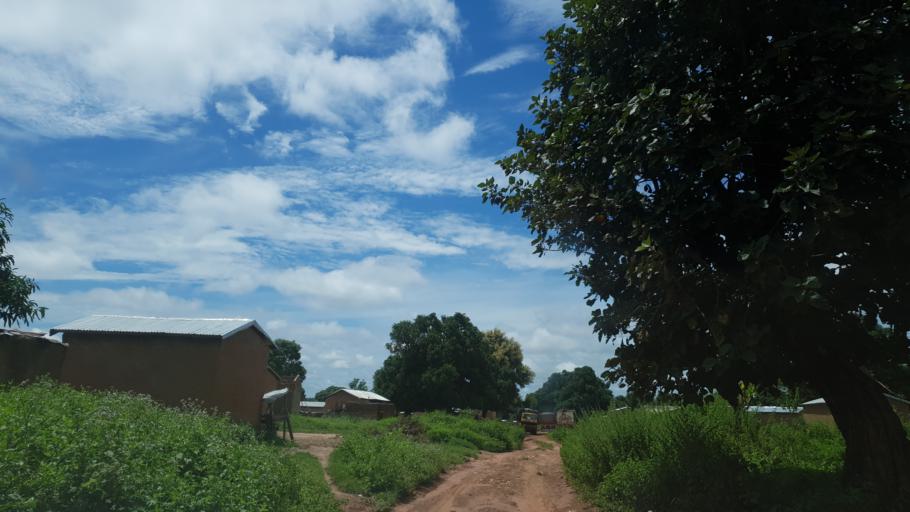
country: CI
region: Savanes
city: Tengrela
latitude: 10.3617
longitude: -6.9194
